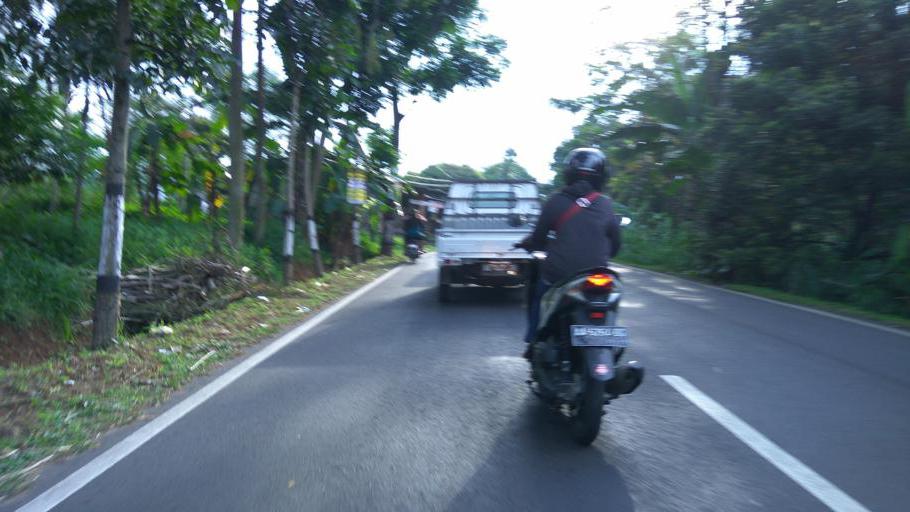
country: ID
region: Central Java
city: Salatiga
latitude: -7.3683
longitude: 110.4578
